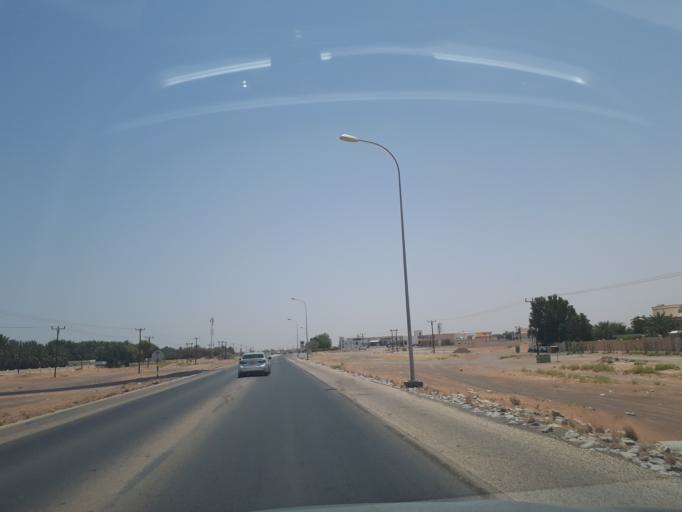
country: OM
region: Ash Sharqiyah
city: Badiyah
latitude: 22.4954
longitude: 58.7555
